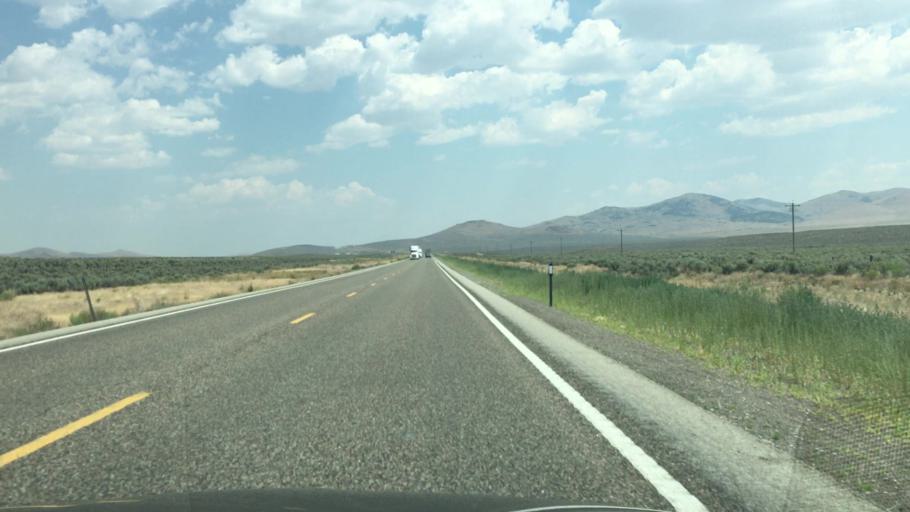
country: US
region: Nevada
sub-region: Elko County
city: Wells
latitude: 41.1509
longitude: -114.9029
